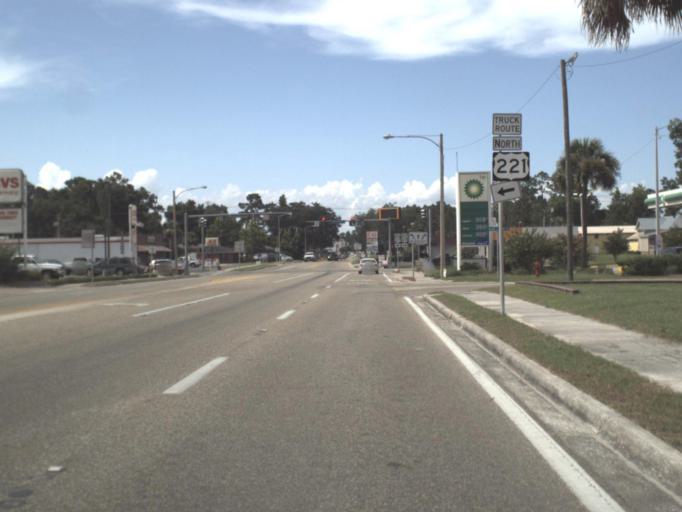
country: US
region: Florida
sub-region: Taylor County
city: Perry
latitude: 30.1105
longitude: -83.5820
